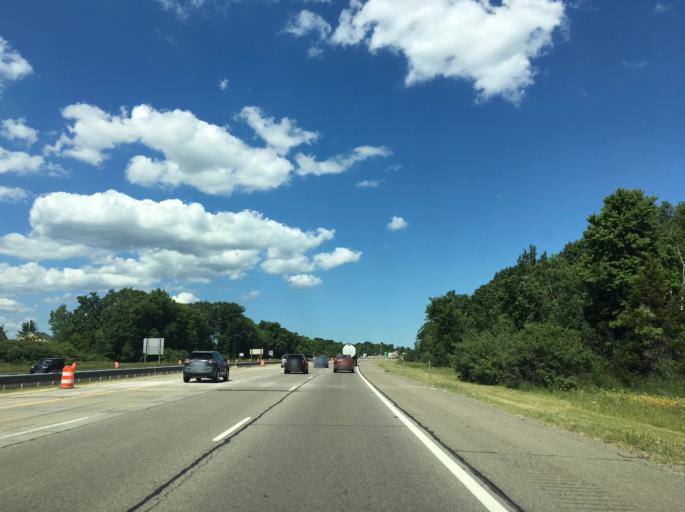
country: US
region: Michigan
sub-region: Oakland County
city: Pontiac
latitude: 42.7056
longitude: -83.3196
